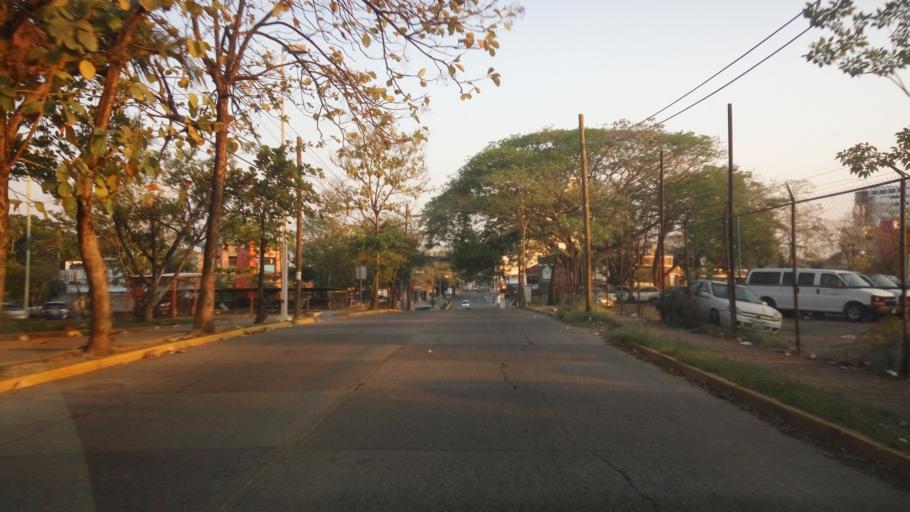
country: MX
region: Tabasco
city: Villahermosa
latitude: 18.0024
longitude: -92.9420
